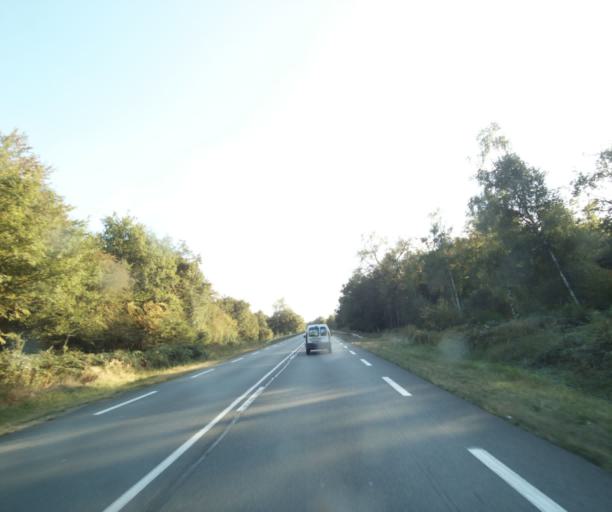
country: FR
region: Bourgogne
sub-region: Departement de Saone-et-Loire
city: Palinges
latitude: 46.5350
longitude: 4.1692
